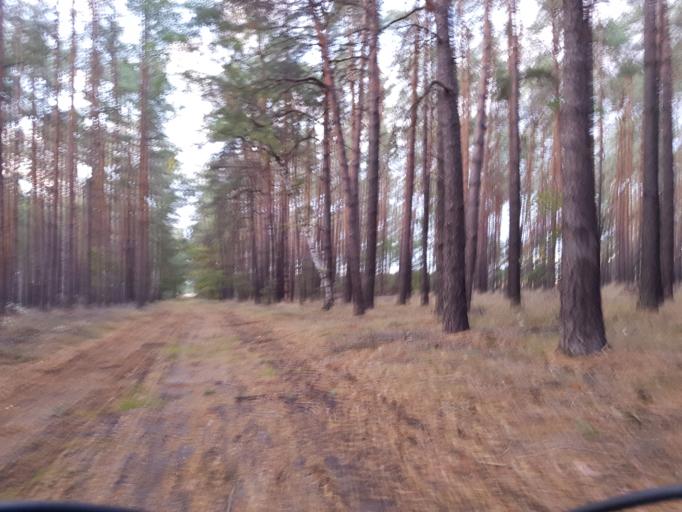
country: DE
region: Brandenburg
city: Schilda
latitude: 51.6042
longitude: 13.3644
